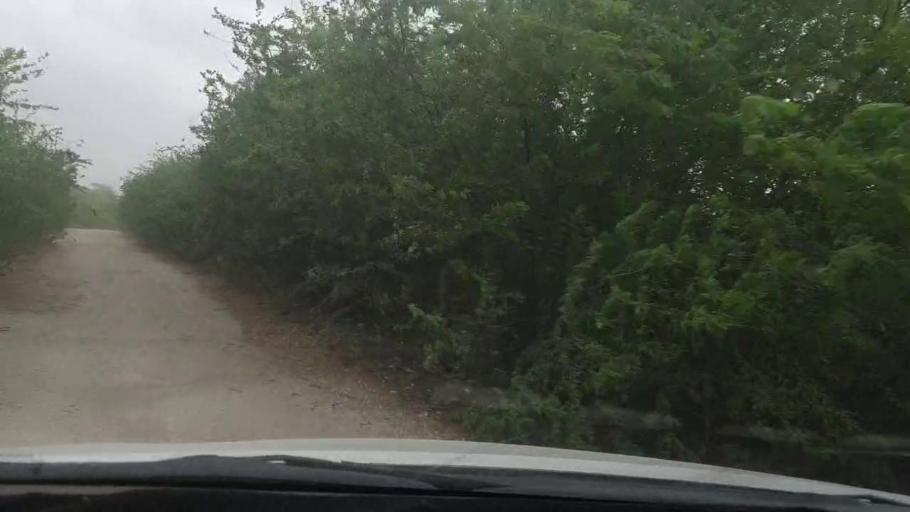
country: PK
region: Sindh
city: Khairpur
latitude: 27.4437
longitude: 68.9877
